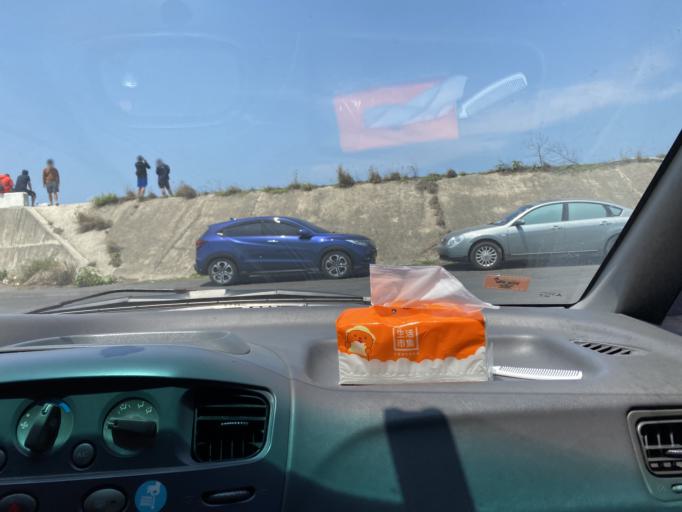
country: TW
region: Taiwan
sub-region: Changhua
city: Chang-hua
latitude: 24.0316
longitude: 120.3684
